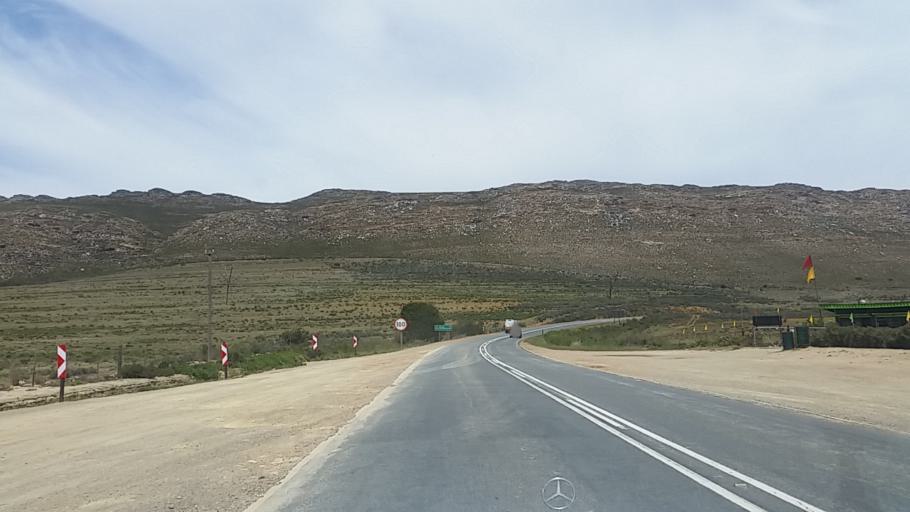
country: ZA
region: Western Cape
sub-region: Eden District Municipality
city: Knysna
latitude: -33.7365
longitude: 23.0397
